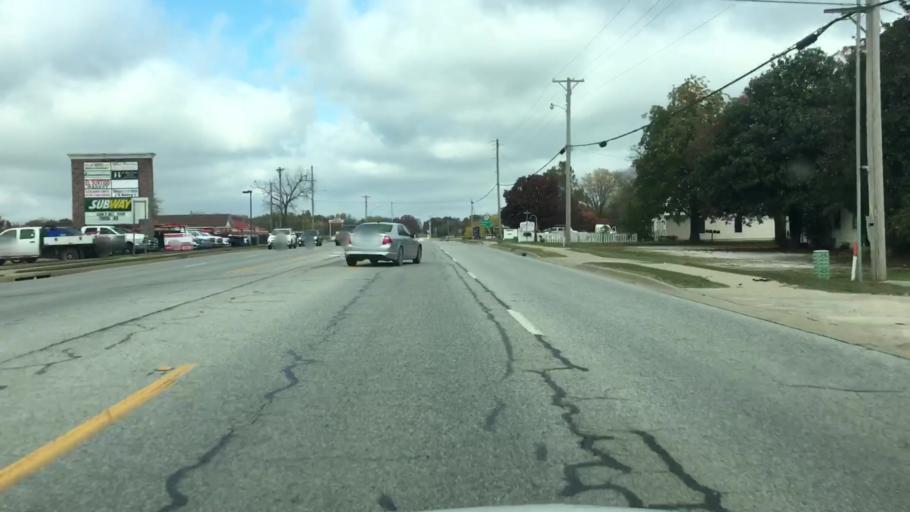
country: US
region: Arkansas
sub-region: Benton County
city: Gentry
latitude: 36.2570
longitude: -94.4852
